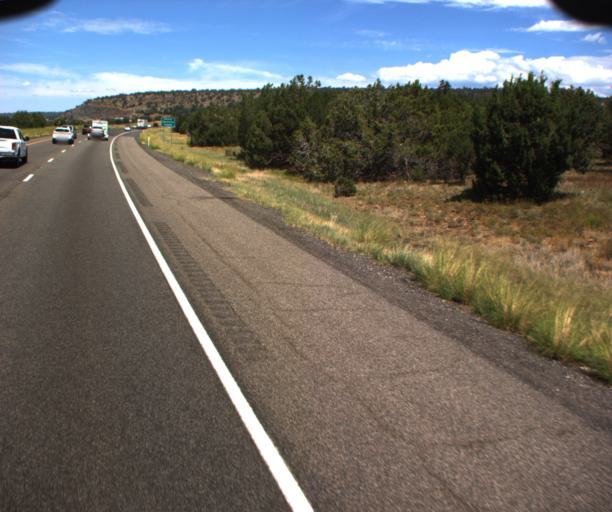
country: US
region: Arizona
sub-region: Yavapai County
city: Village of Oak Creek (Big Park)
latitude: 34.8018
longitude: -111.5952
